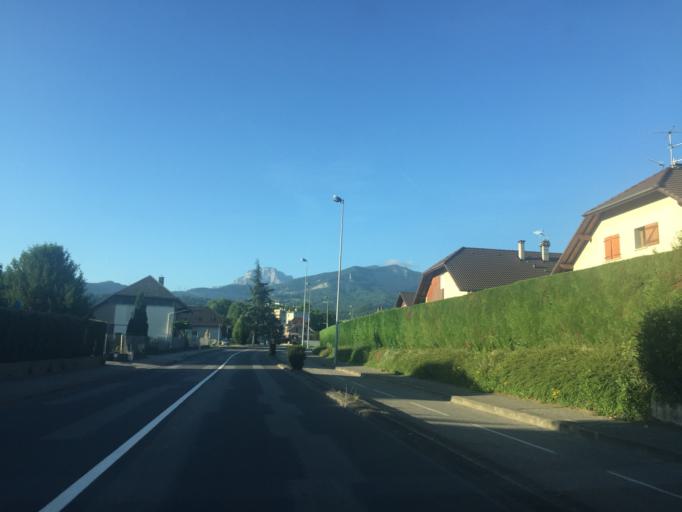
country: FR
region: Rhone-Alpes
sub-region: Departement de la Savoie
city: Cognin
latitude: 45.5668
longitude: 5.8931
